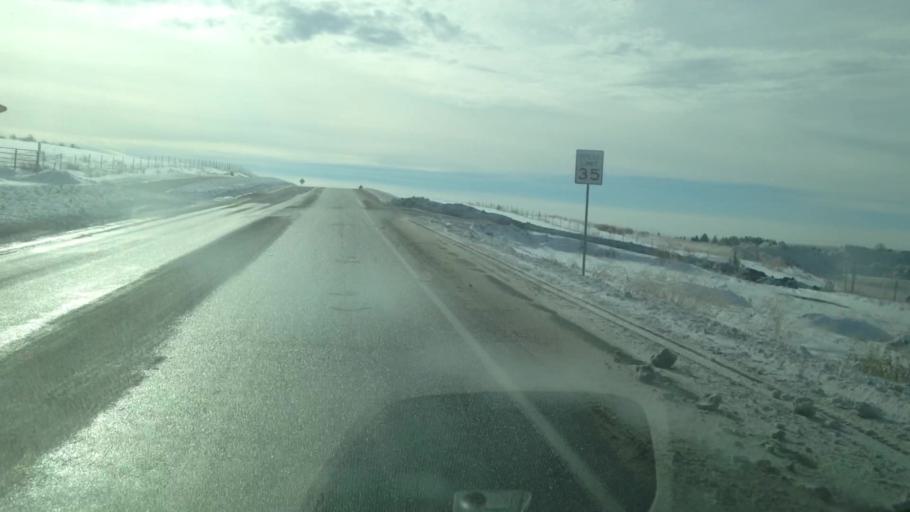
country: US
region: Idaho
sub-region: Madison County
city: Rexburg
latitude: 43.8086
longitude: -111.7895
